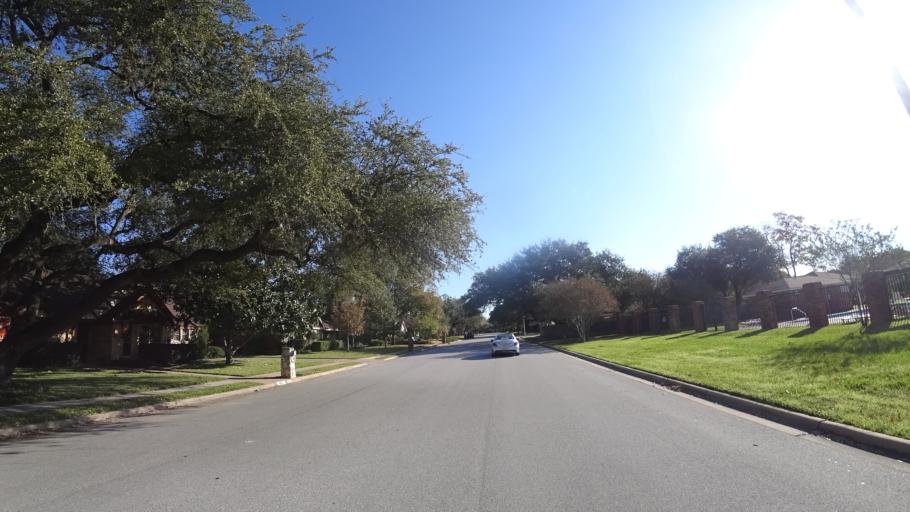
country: US
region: Texas
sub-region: Travis County
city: Shady Hollow
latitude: 30.2207
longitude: -97.8507
